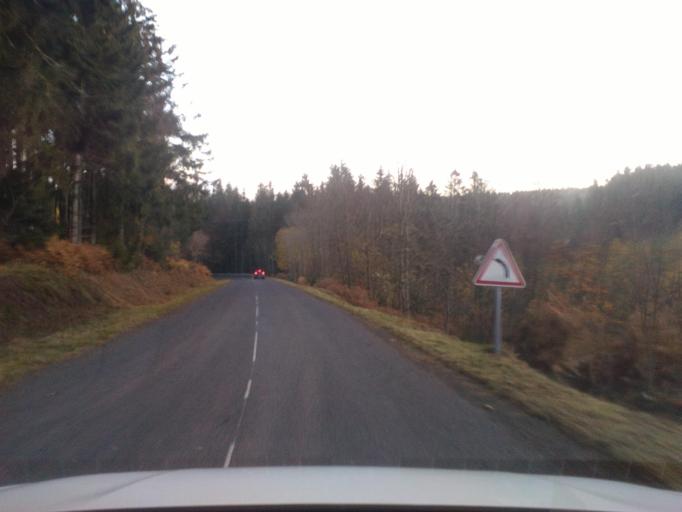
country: FR
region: Lorraine
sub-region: Departement des Vosges
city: Senones
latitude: 48.3869
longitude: 7.0955
